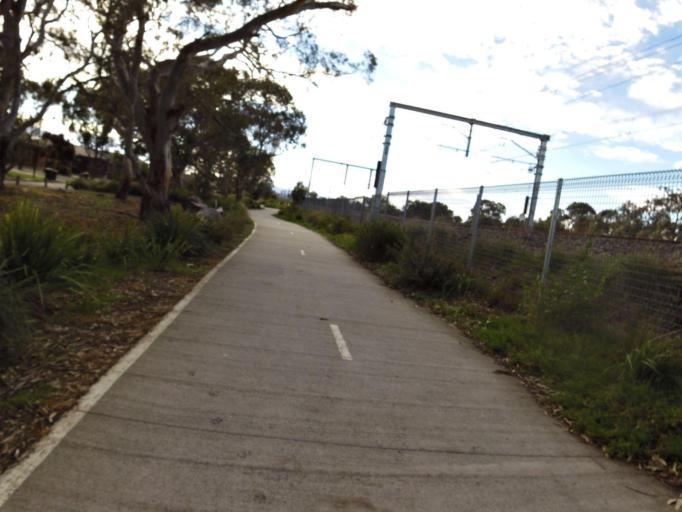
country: AU
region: Victoria
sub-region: Whittlesea
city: Mernda
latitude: -37.6131
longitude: 145.0985
